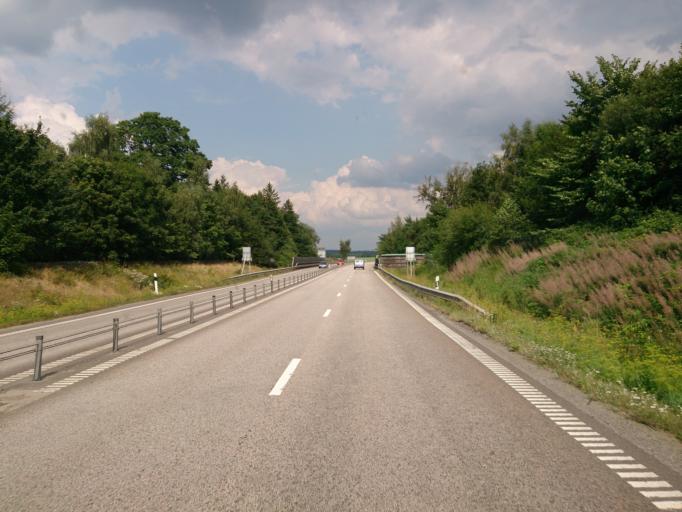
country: SE
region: Skane
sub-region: Horby Kommun
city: Hoerby
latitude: 55.8492
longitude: 13.6026
